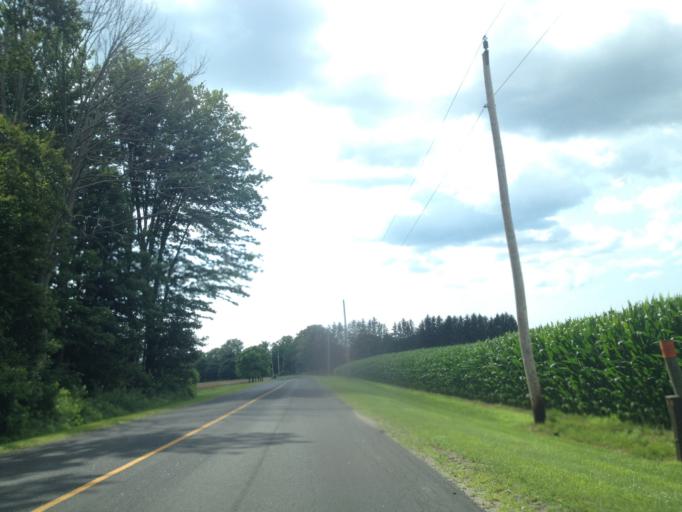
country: CA
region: Ontario
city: Aylmer
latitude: 42.6767
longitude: -81.0209
